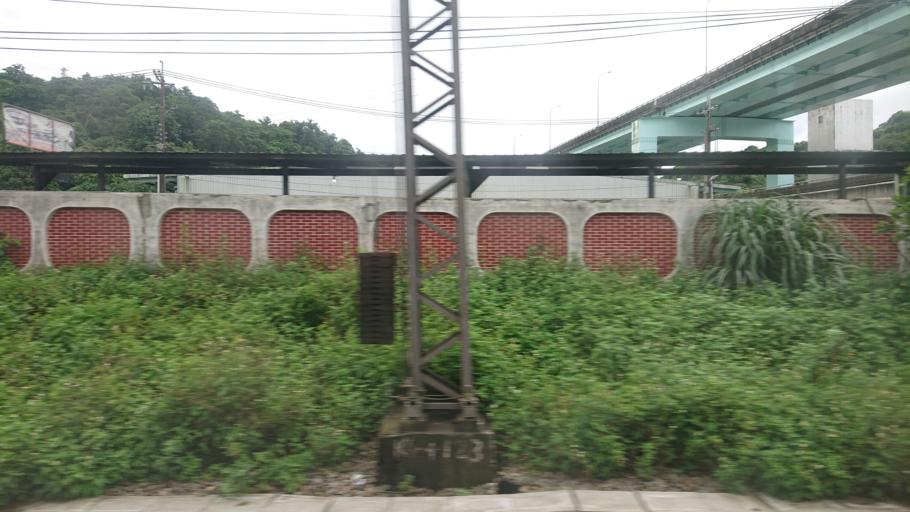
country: TW
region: Taiwan
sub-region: Keelung
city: Keelung
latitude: 25.1055
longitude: 121.7260
